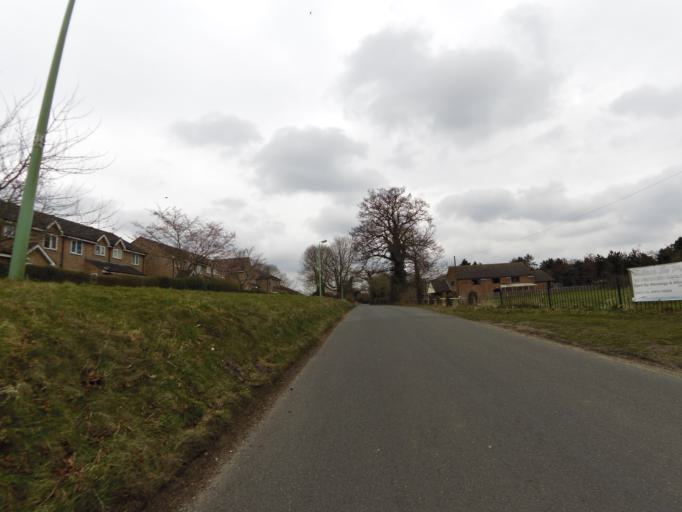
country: GB
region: England
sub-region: Suffolk
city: Halesworth
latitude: 52.3459
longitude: 1.5228
